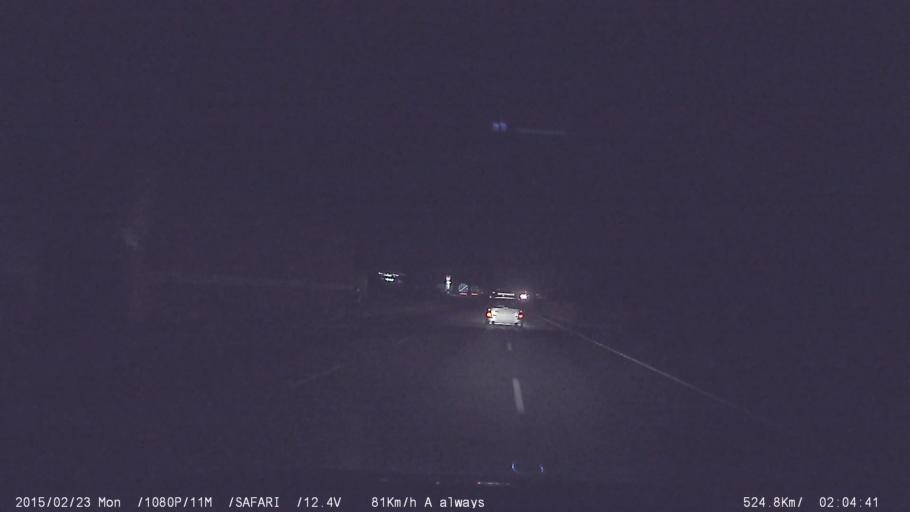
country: IN
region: Tamil Nadu
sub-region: Krishnagiri
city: Kelamangalam
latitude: 12.6491
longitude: 78.0379
